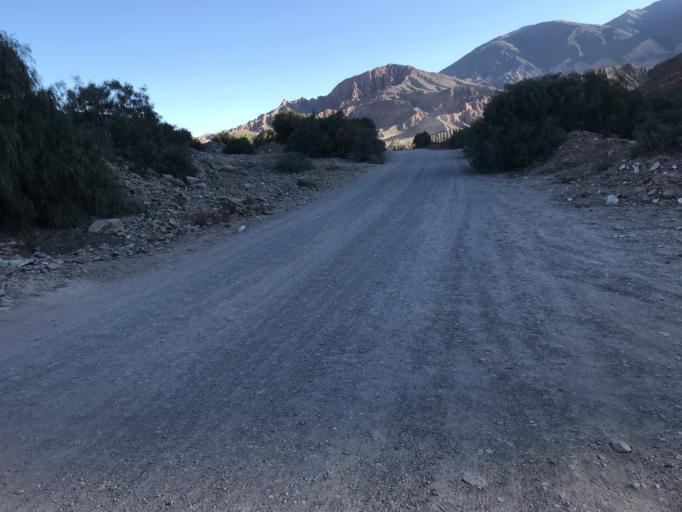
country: AR
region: Jujuy
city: Maimara
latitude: -23.5793
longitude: -65.4020
